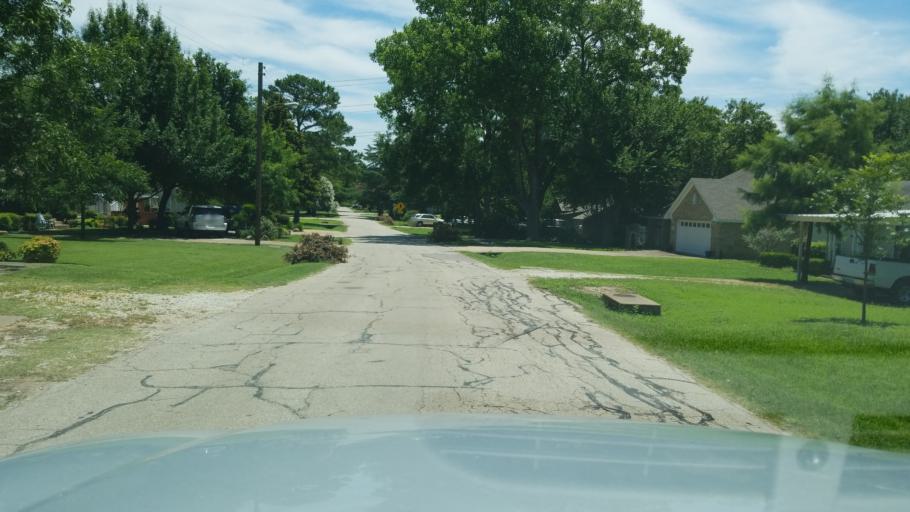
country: US
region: Texas
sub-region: Dallas County
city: Irving
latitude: 32.8041
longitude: -96.9135
